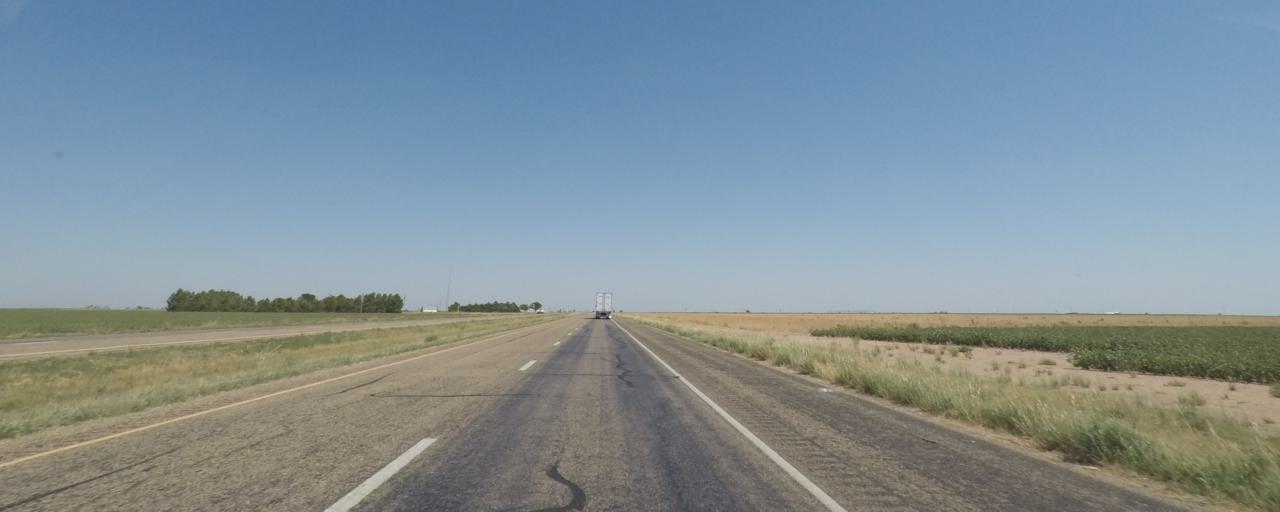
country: US
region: Texas
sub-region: Crosby County
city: Ralls
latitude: 33.6693
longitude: -101.3468
